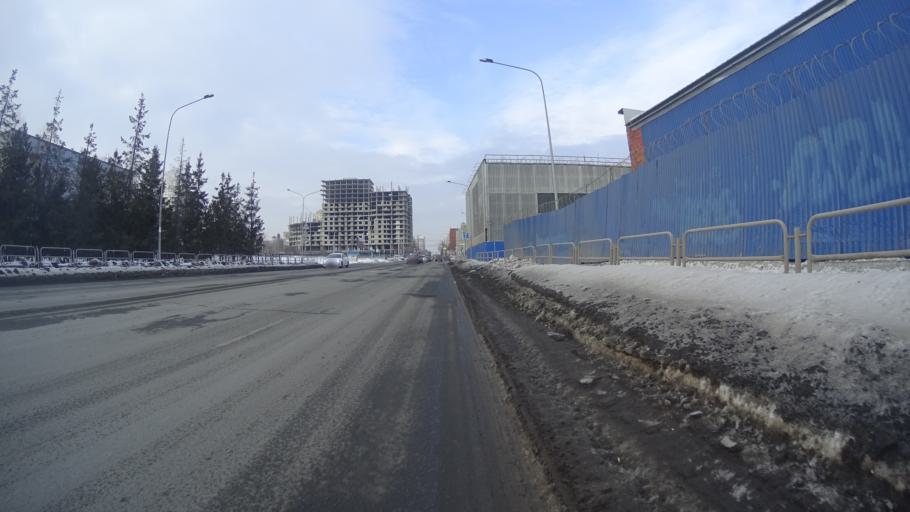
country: RU
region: Chelyabinsk
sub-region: Gorod Chelyabinsk
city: Chelyabinsk
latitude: 55.1724
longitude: 61.3951
